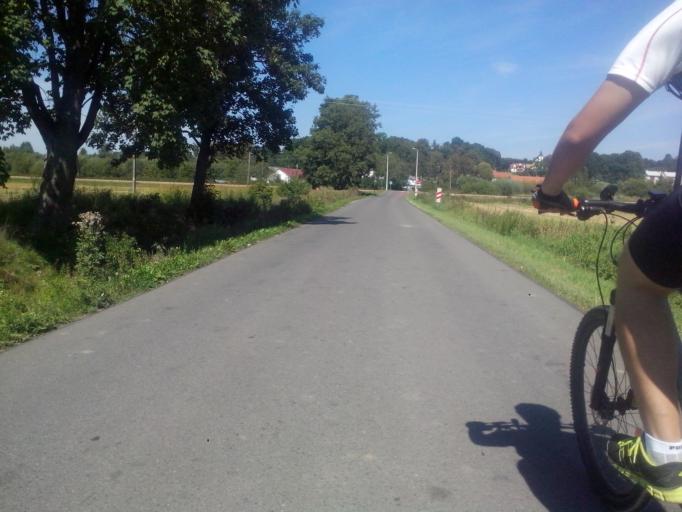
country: PL
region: Subcarpathian Voivodeship
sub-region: Powiat strzyzowski
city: Wisniowa
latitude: 49.8632
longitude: 21.6475
